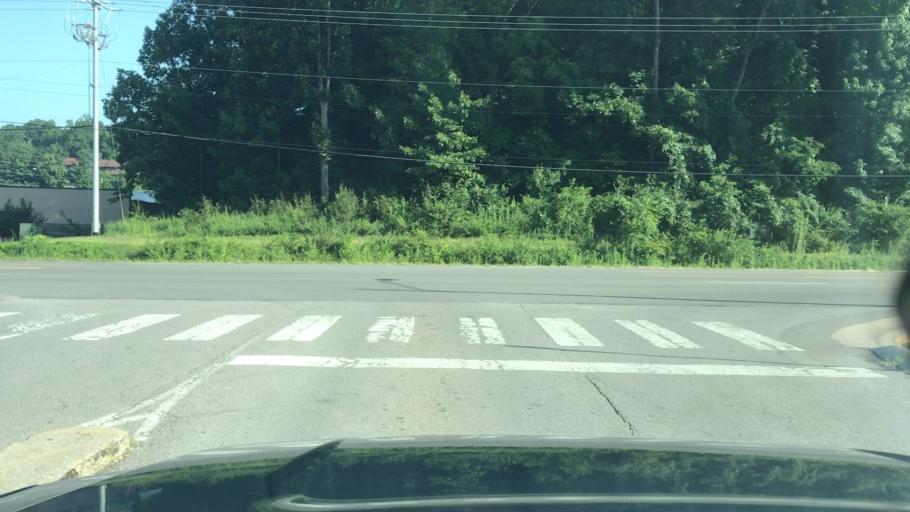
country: US
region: Tennessee
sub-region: Davidson County
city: Belle Meade
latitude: 36.0750
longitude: -86.9186
